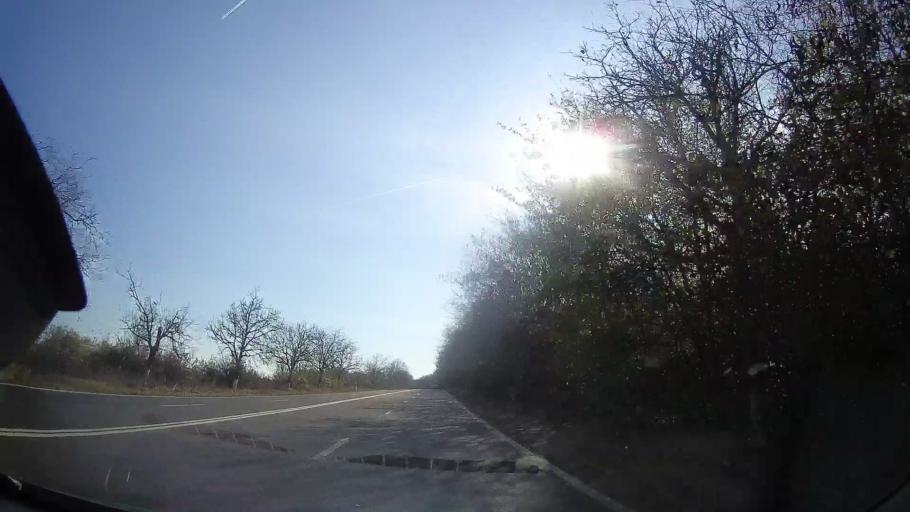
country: RO
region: Constanta
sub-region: Comuna Douazeci si Trei August
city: Dulcesti
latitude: 43.8864
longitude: 28.5732
